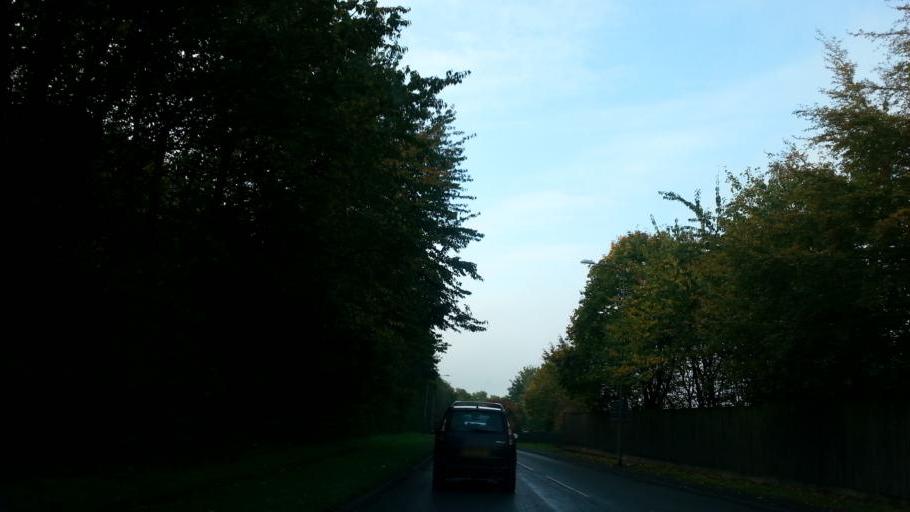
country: GB
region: England
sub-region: Worcestershire
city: Bromsgrove
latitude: 52.3214
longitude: -2.0600
